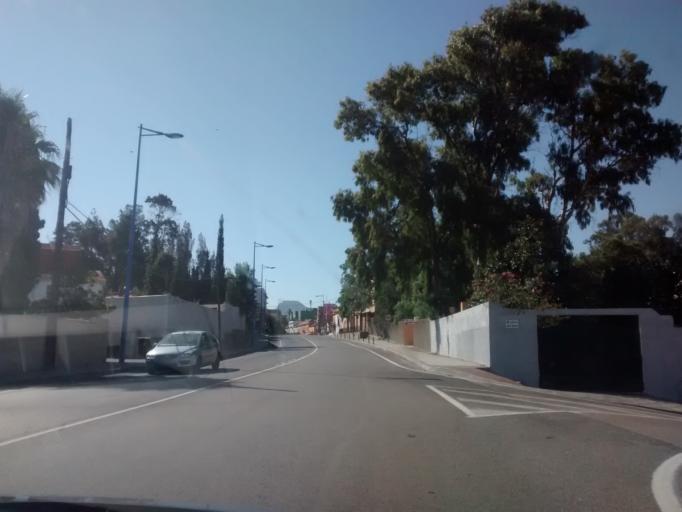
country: ES
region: Andalusia
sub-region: Provincia de Cadiz
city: San Roque
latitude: 36.1800
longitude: -5.3796
